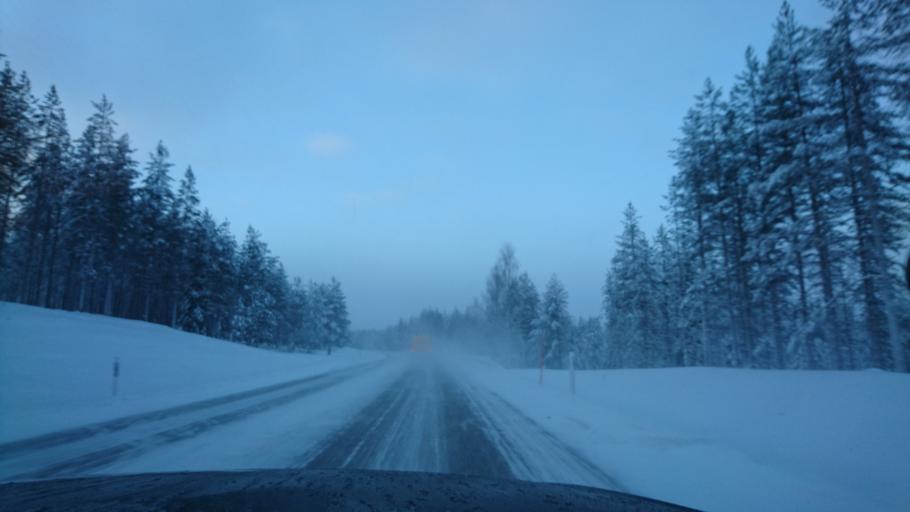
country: FI
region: Northern Ostrobothnia
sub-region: Koillismaa
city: Taivalkoski
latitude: 65.4848
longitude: 27.8180
